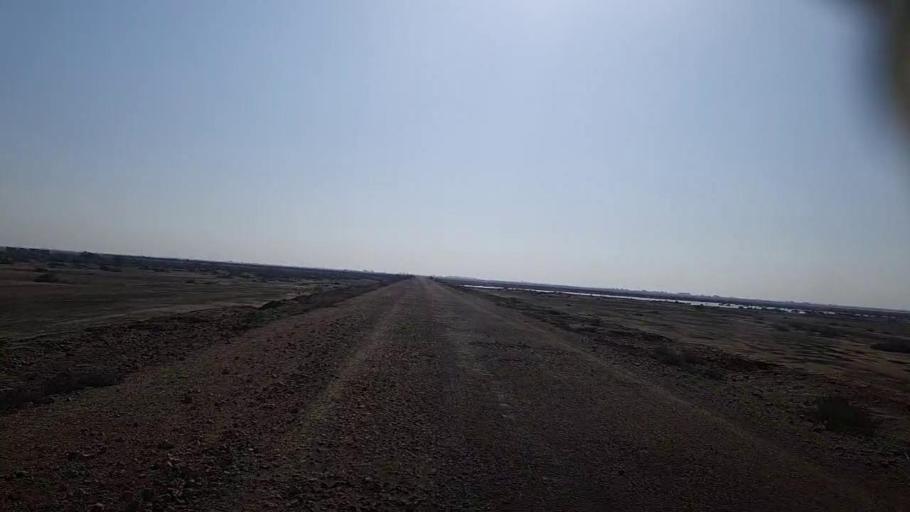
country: PK
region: Sindh
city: Mirpur Sakro
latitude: 24.5197
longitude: 67.4900
